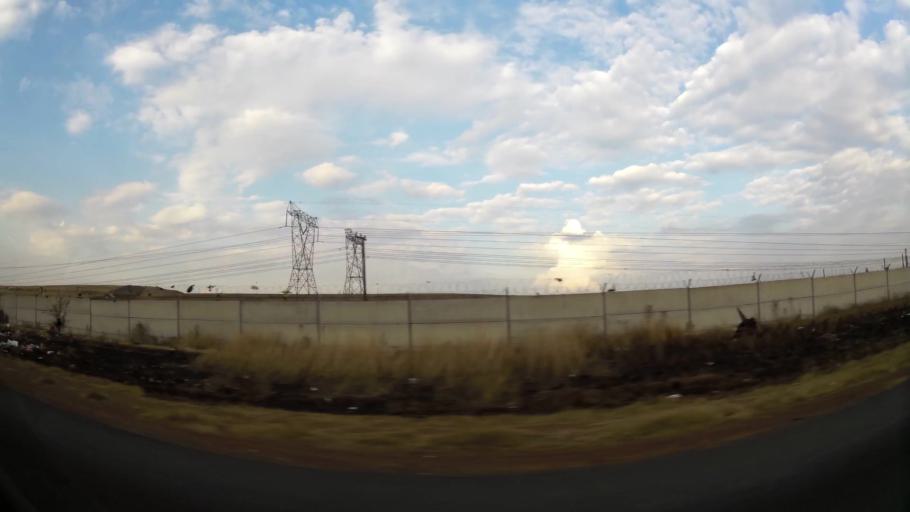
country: ZA
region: Gauteng
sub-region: Sedibeng District Municipality
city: Vanderbijlpark
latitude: -26.6420
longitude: 27.8051
